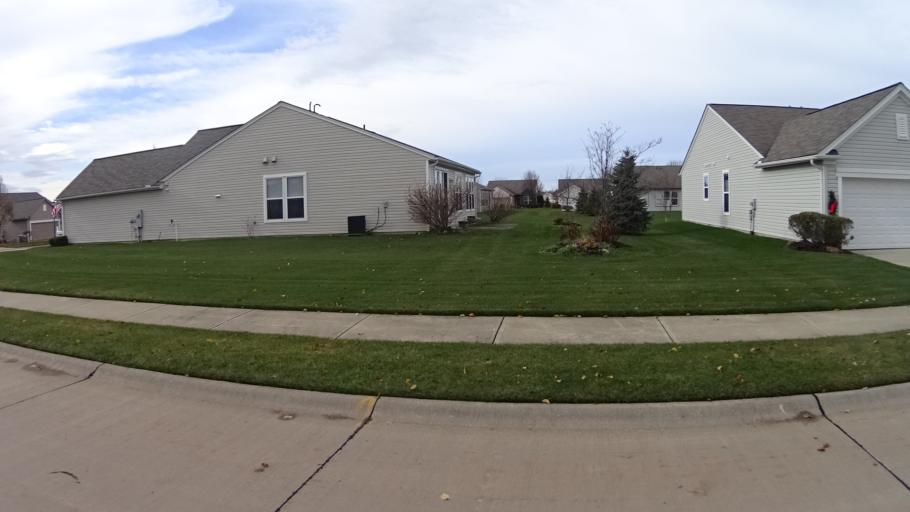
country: US
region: Ohio
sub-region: Lorain County
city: North Ridgeville
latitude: 41.3558
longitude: -82.0514
